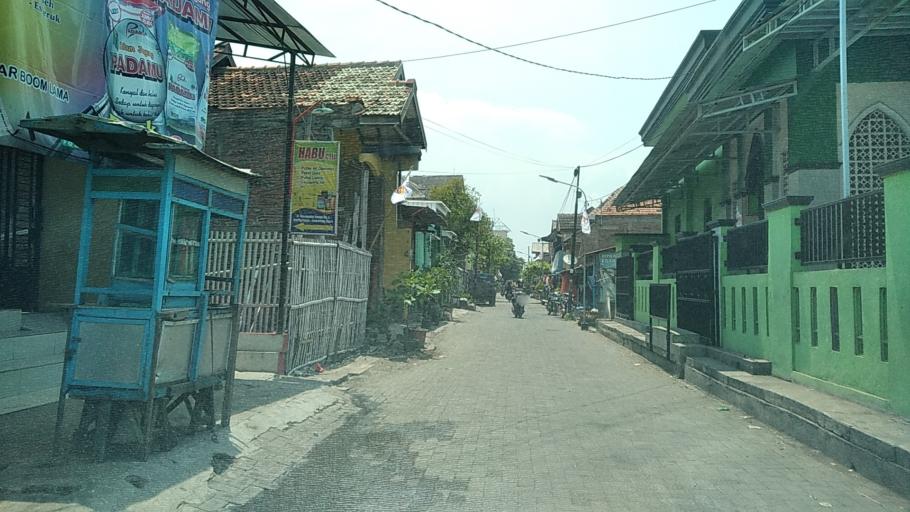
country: ID
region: Central Java
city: Semarang
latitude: -6.9567
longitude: 110.4187
